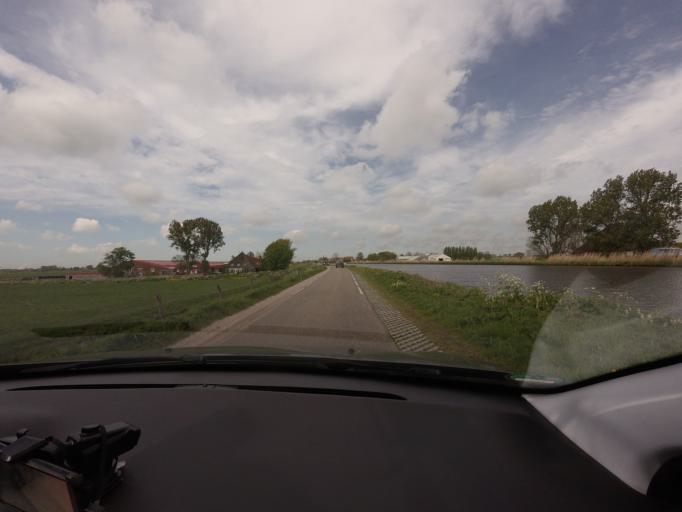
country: NL
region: North Holland
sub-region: Gemeente Zaanstad
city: Zaanstad
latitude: 52.5428
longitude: 4.8234
